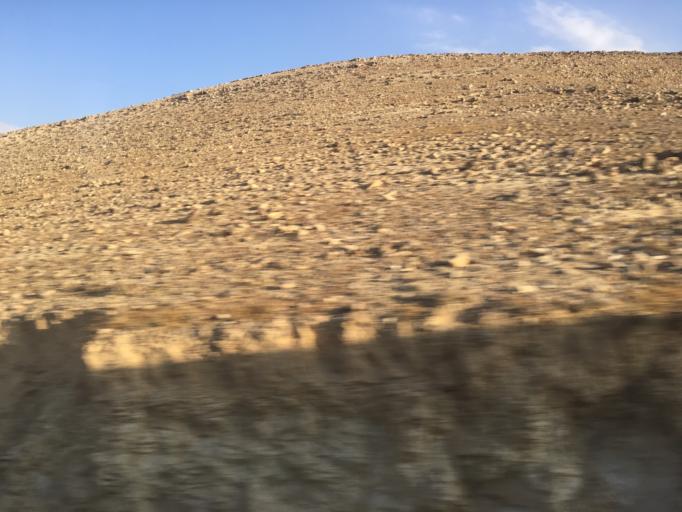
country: IL
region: Southern District
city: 'Arad
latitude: 31.3069
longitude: 35.2542
